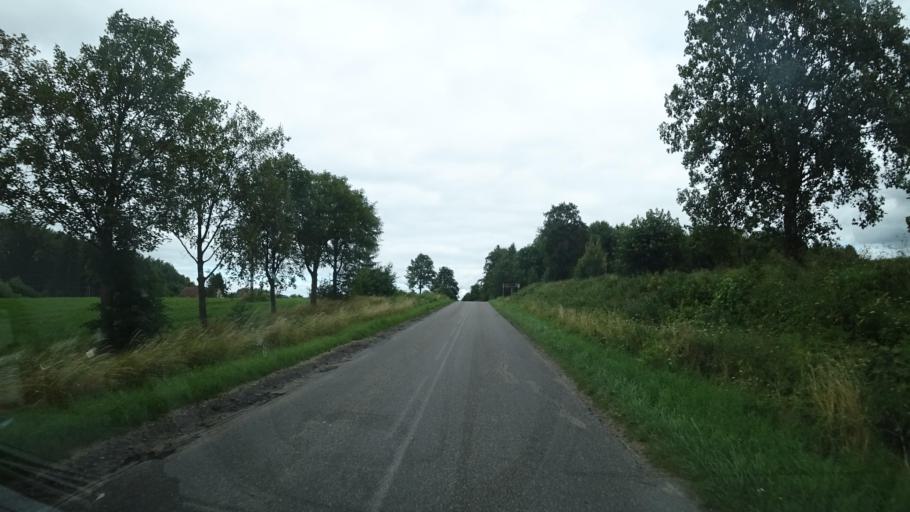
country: PL
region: Podlasie
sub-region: Powiat suwalski
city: Filipow
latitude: 54.2824
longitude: 22.5361
